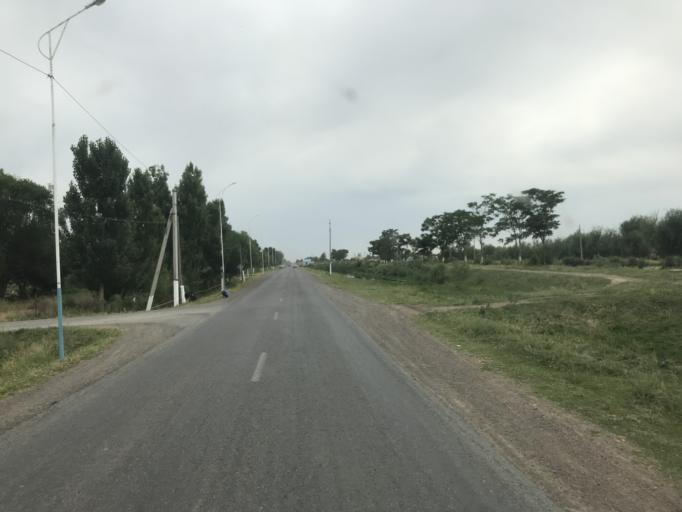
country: KZ
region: Ongtustik Qazaqstan
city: Asykata
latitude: 40.9381
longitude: 68.4123
